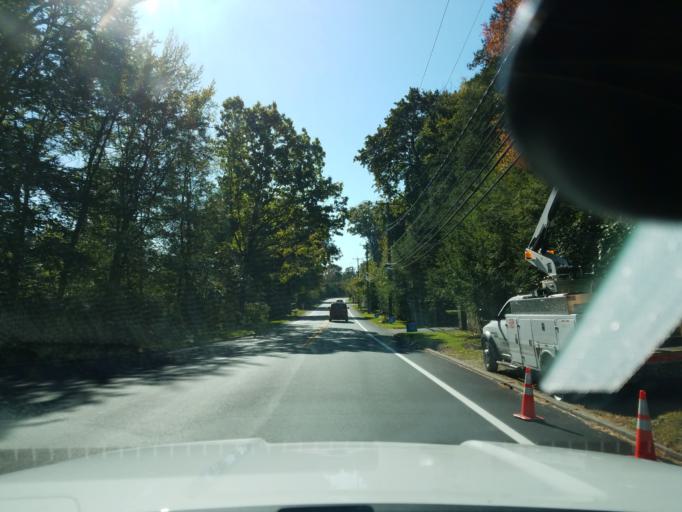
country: US
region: Connecticut
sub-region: Fairfield County
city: Cos Cob
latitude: 41.0570
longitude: -73.6174
